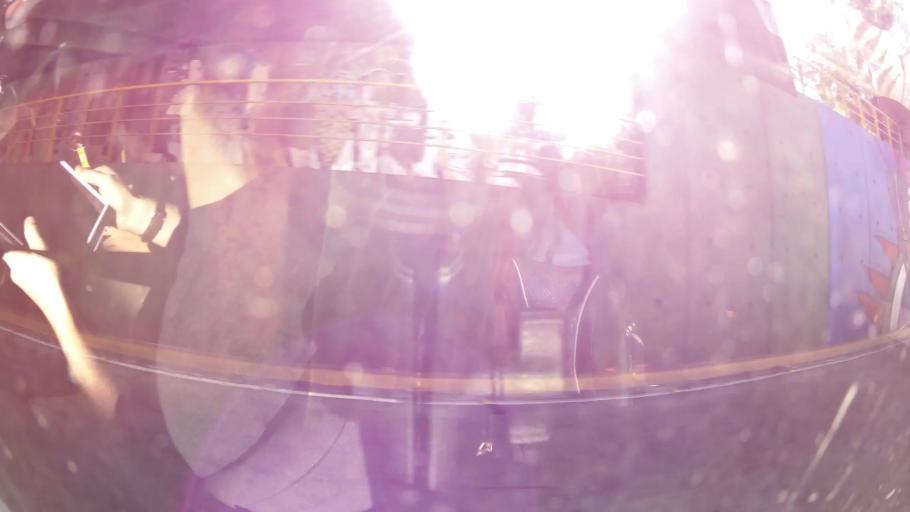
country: AR
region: Buenos Aires
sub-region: Partido de General San Martin
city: General San Martin
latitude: -34.5405
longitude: -58.5064
